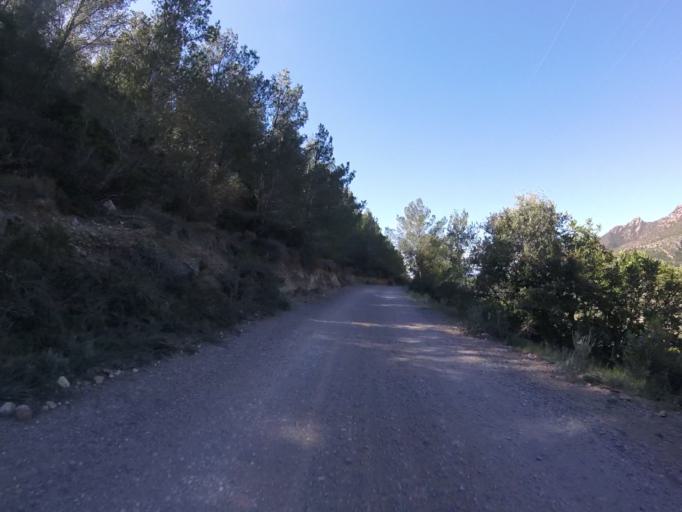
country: ES
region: Valencia
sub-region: Provincia de Castello
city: Benicassim
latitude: 40.0780
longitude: 0.0793
